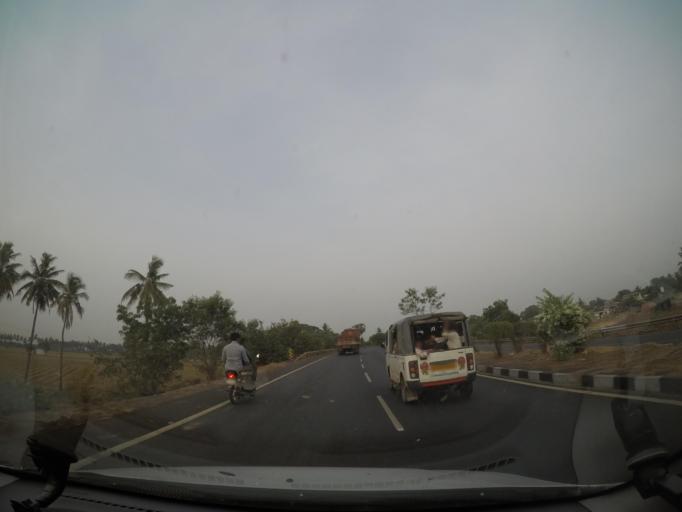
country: IN
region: Andhra Pradesh
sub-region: Krishna
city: Gannavaram
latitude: 16.6102
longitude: 80.9220
